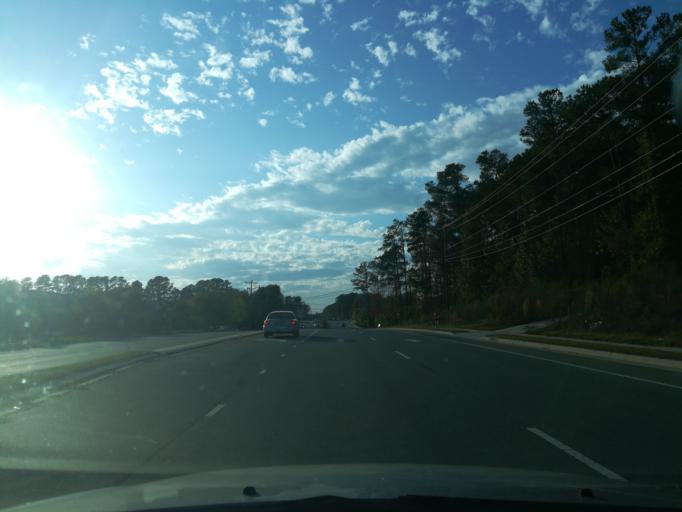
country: US
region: North Carolina
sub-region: Orange County
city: Chapel Hill
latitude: 35.9640
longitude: -79.0534
